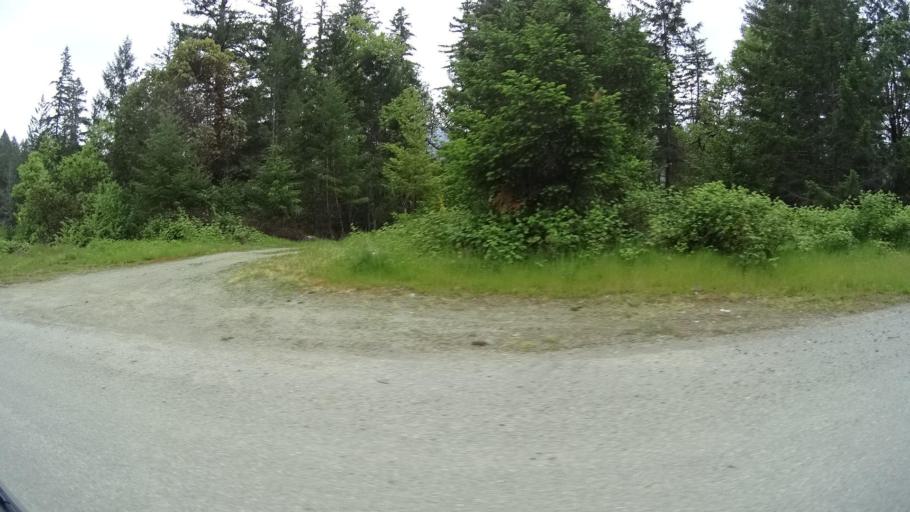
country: US
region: California
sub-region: Humboldt County
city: Willow Creek
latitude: 41.1203
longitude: -123.7407
